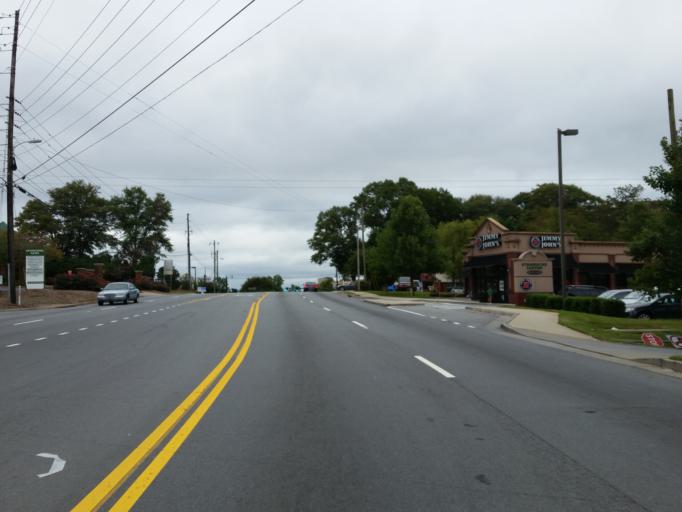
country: US
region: Georgia
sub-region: Cobb County
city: Marietta
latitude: 33.9722
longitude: -84.5509
